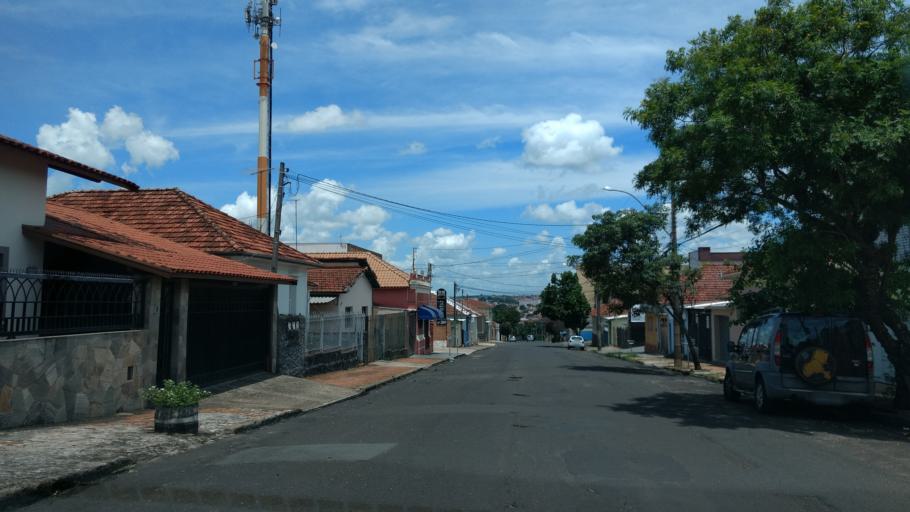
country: BR
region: Sao Paulo
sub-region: Botucatu
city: Botucatu
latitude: -22.8716
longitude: -48.4506
